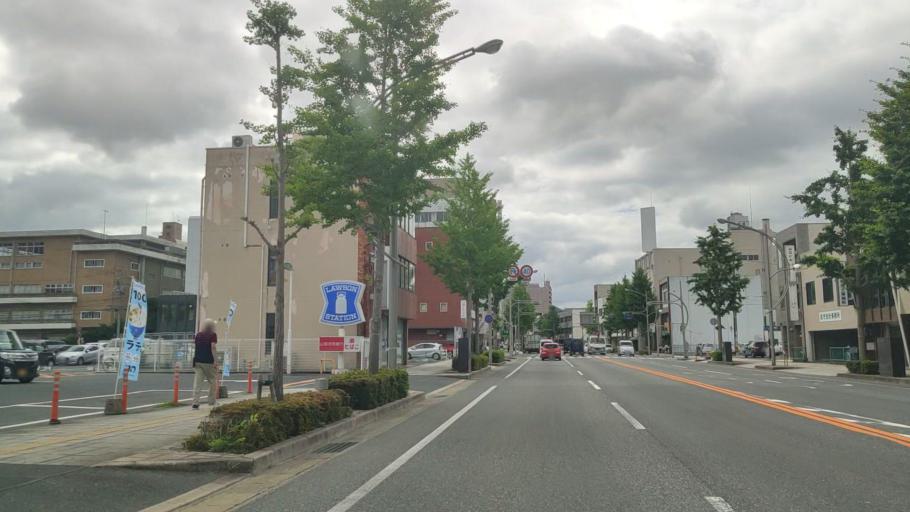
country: JP
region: Tottori
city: Yonago
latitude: 35.4269
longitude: 133.3299
